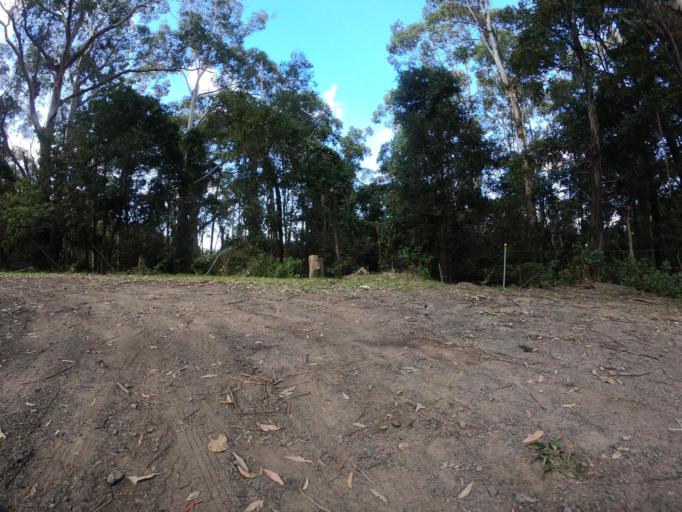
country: AU
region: New South Wales
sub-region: Wollongong
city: Cordeaux Heights
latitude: -34.4138
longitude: 150.8163
